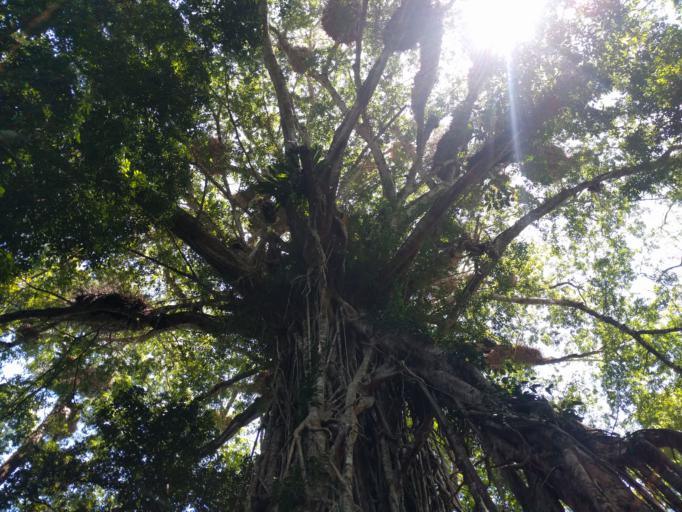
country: AU
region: Queensland
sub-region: Tablelands
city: Tolga
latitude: -17.2131
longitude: 145.6988
